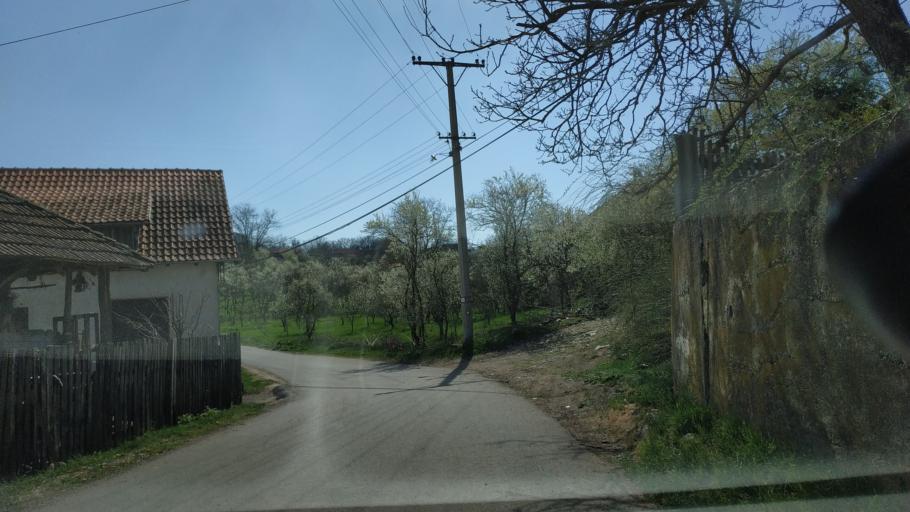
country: RS
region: Central Serbia
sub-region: Zajecarski Okrug
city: Soko Banja
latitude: 43.5699
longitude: 21.9021
